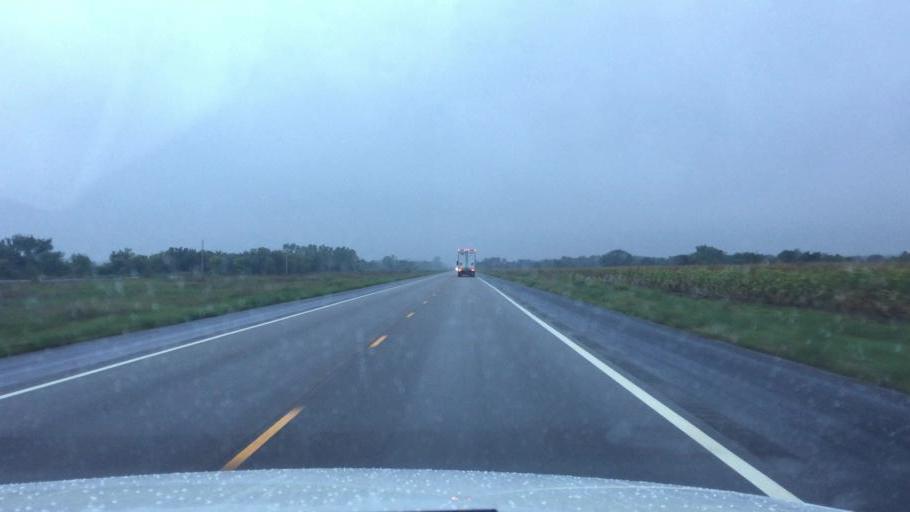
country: US
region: Kansas
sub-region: Montgomery County
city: Cherryvale
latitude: 37.4049
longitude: -95.5018
